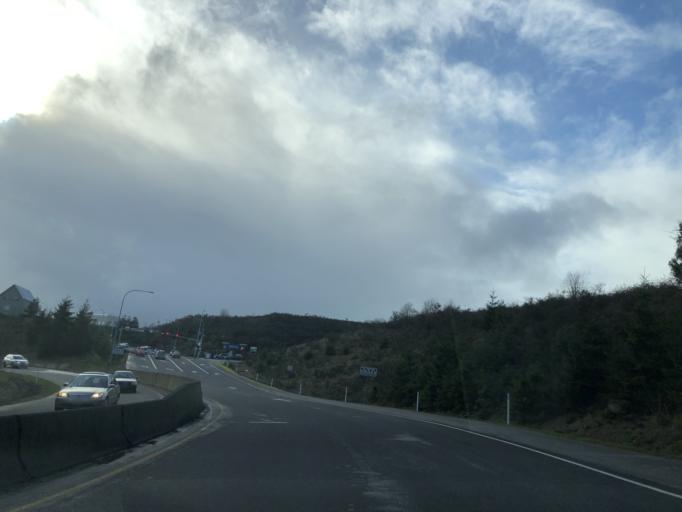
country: US
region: Washington
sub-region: Kitsap County
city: Poulsbo
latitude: 47.7610
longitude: -122.6575
